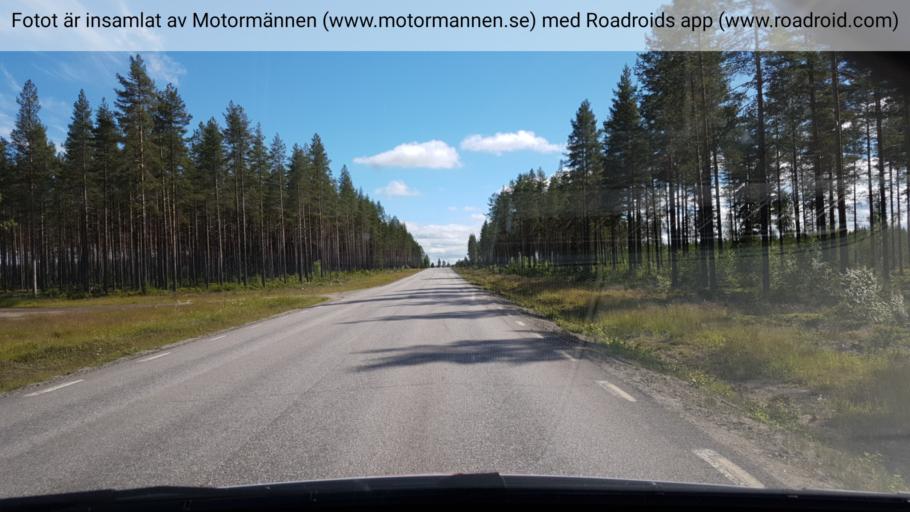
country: SE
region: Vaesterbotten
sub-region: Vindelns Kommun
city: Vindeln
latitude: 64.0789
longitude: 19.6334
